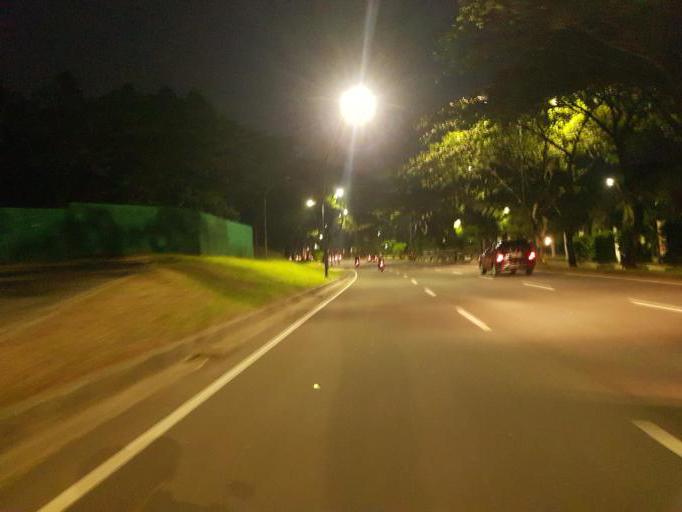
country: ID
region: West Java
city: Serpong
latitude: -6.2989
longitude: 106.6572
